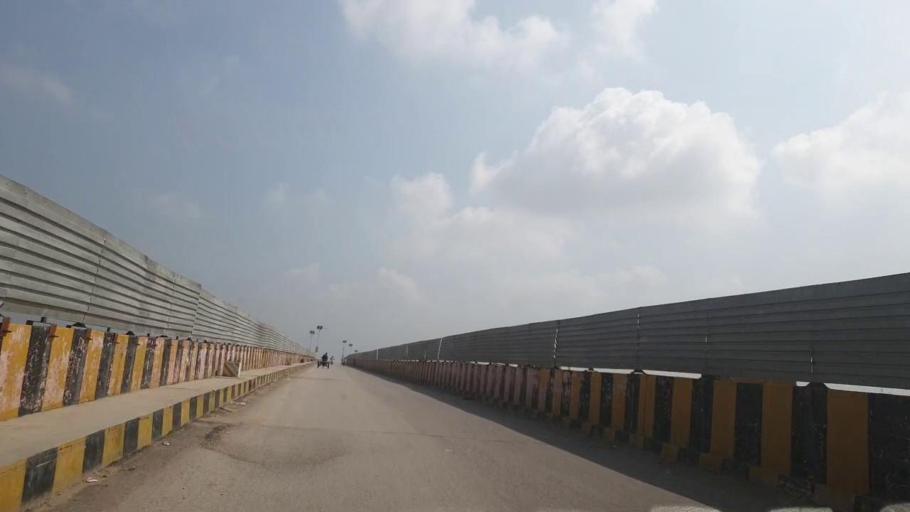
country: PK
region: Sindh
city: Khairpur
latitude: 27.5253
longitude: 68.7427
